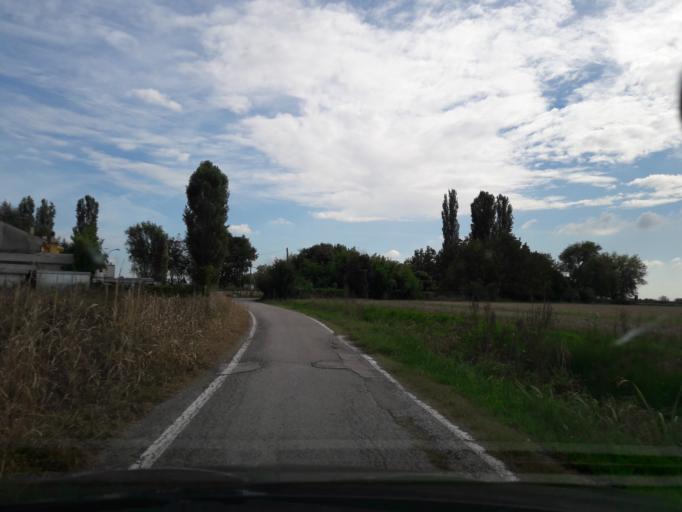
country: IT
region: Veneto
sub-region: Provincia di Padova
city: Piacenza d'Adige
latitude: 45.0880
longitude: 11.5528
